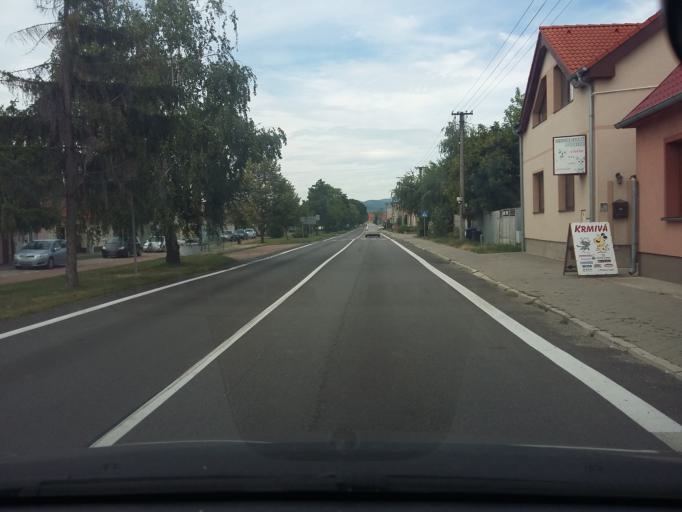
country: SK
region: Bratislavsky
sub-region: Okres Pezinok
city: Pezinok
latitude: 48.2684
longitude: 17.3050
